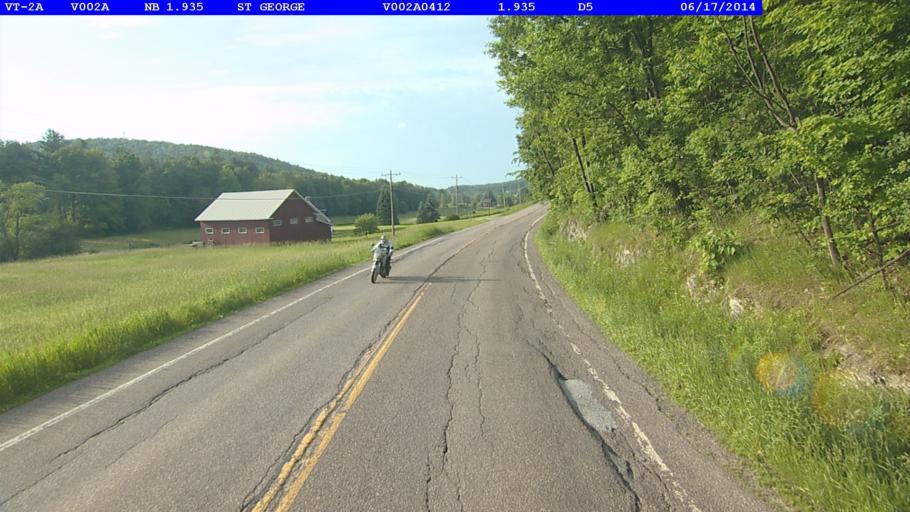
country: US
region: Vermont
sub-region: Chittenden County
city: Hinesburg
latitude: 44.3974
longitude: -73.1279
